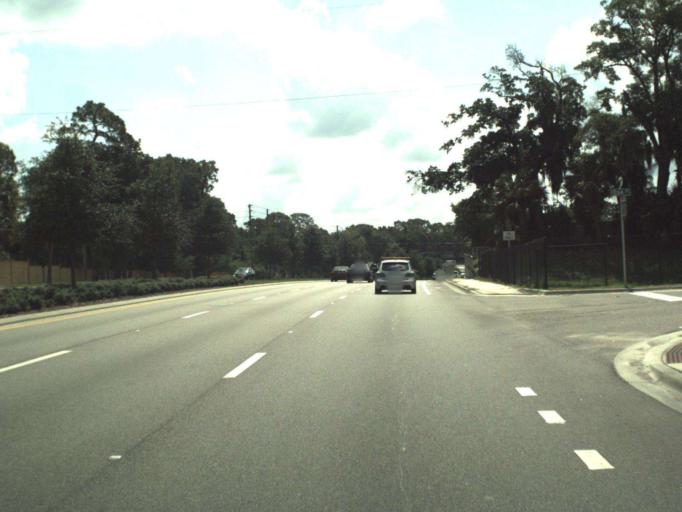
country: US
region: Florida
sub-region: Seminole County
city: Wekiwa Springs
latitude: 28.6871
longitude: -81.4001
